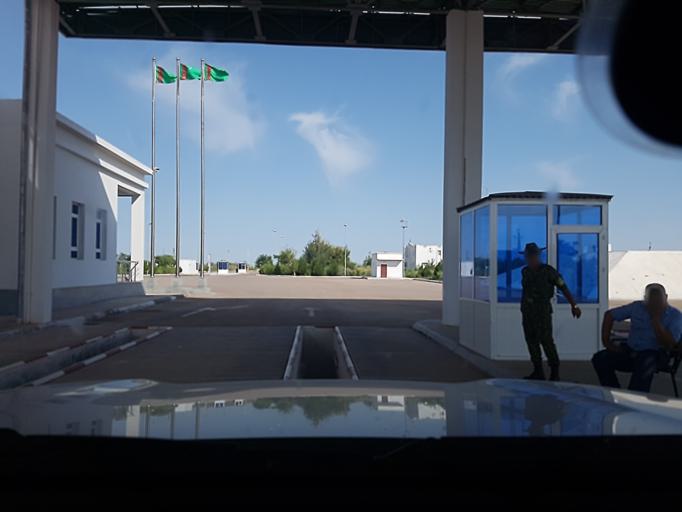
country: TM
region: Dasoguz
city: Dasoguz
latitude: 41.7733
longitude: 60.0590
